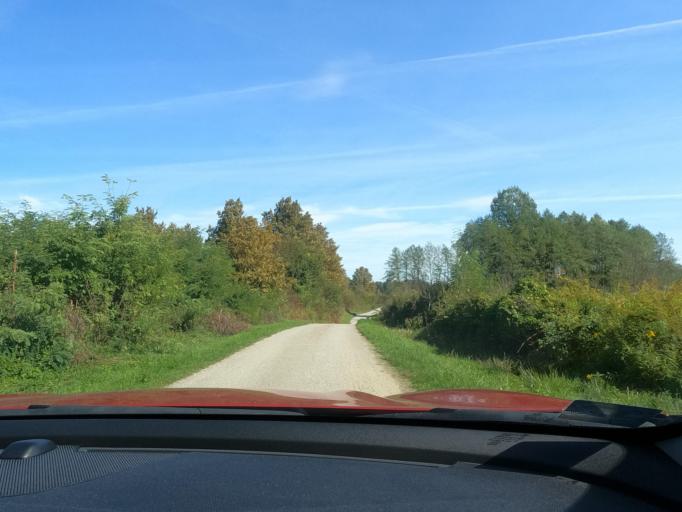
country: HR
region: Sisacko-Moslavacka
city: Petrinja
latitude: 45.3399
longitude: 16.2293
